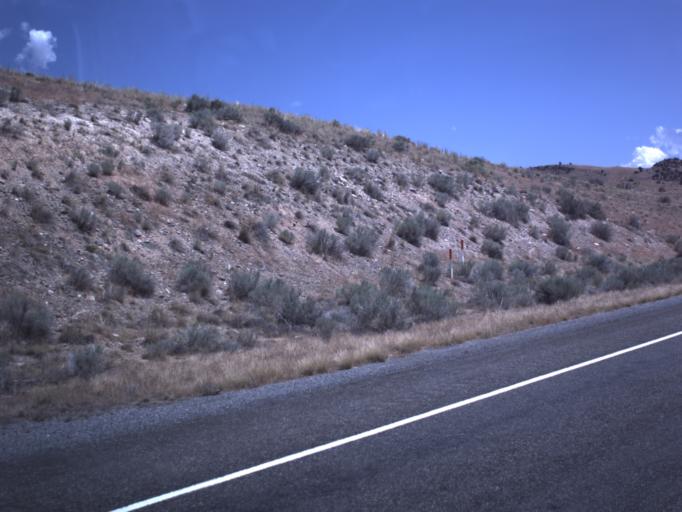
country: US
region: Utah
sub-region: Juab County
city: Nephi
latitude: 39.6361
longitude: -112.1020
